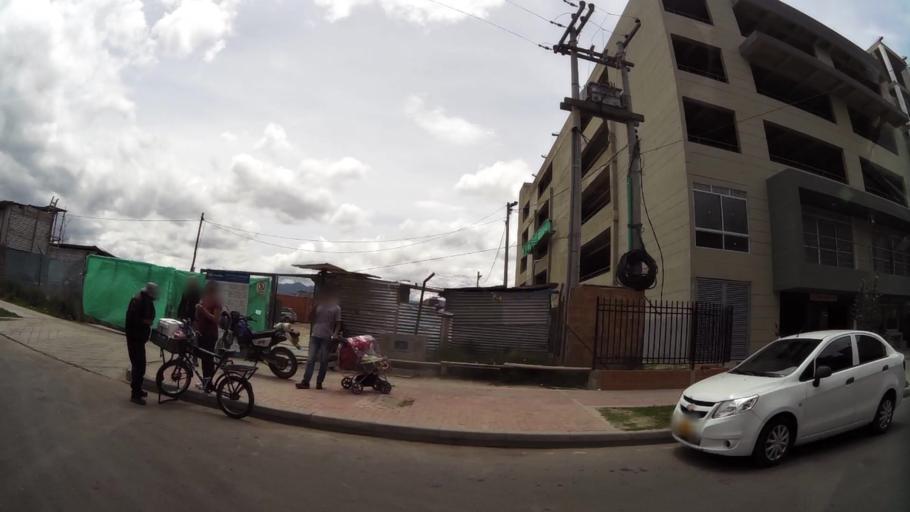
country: CO
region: Bogota D.C.
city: Bogota
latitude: 4.6530
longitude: -74.1530
